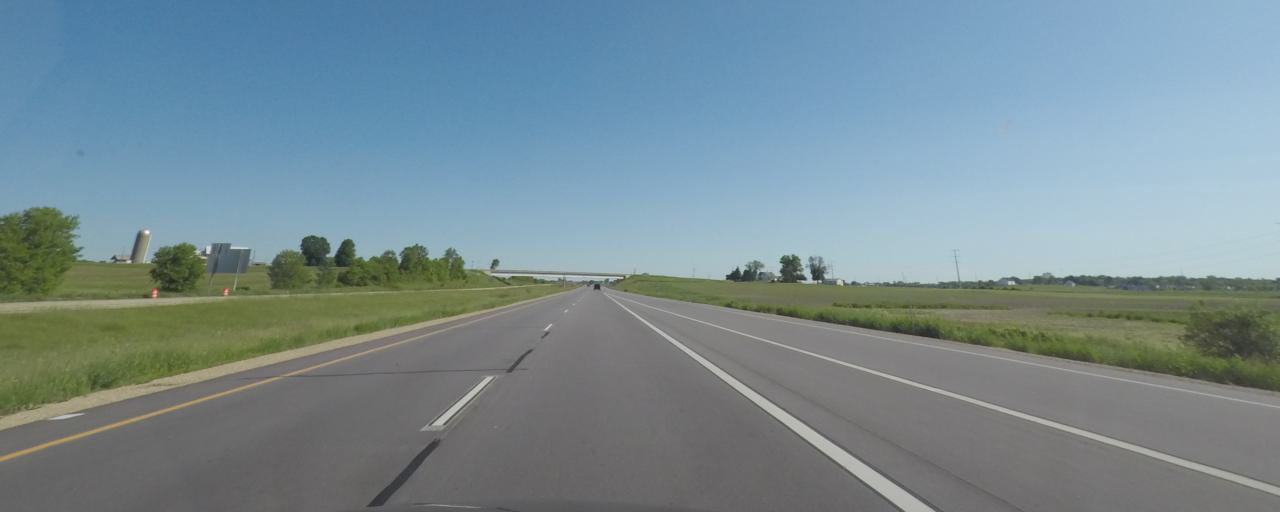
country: US
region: Wisconsin
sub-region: Columbia County
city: Columbus
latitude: 43.3224
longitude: -89.0450
